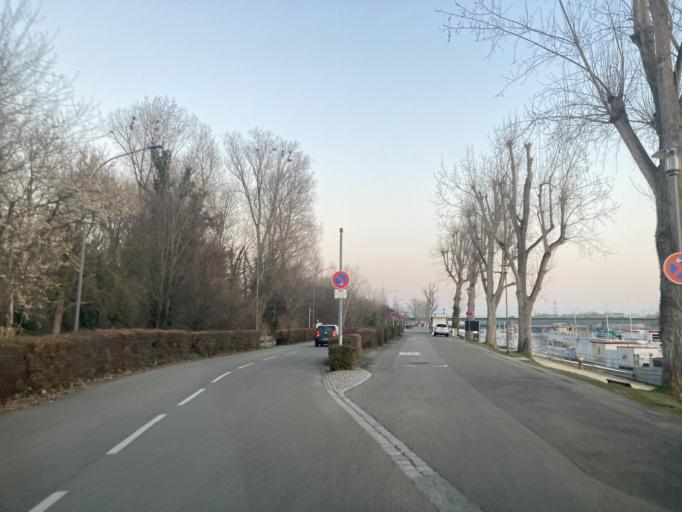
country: DE
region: Baden-Wuerttemberg
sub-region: Freiburg Region
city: Breisach am Rhein
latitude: 48.0265
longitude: 7.5787
